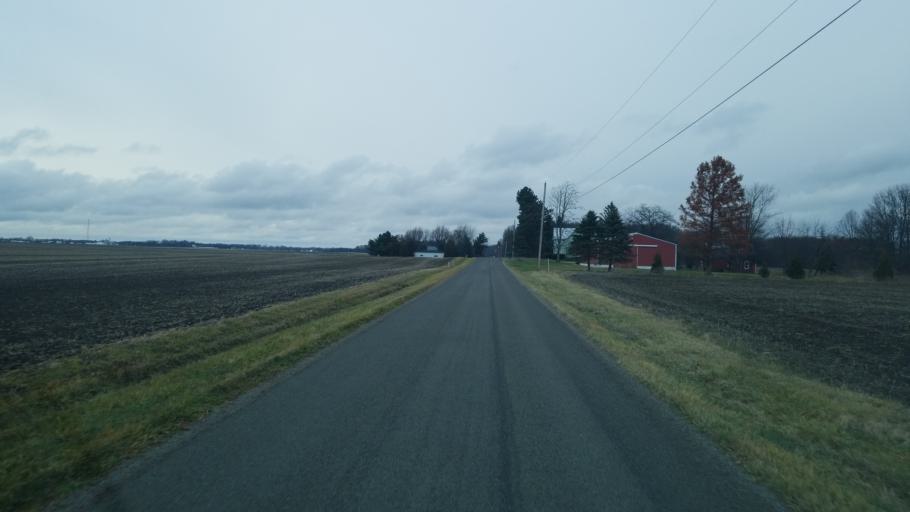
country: US
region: Ohio
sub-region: Union County
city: Richwood
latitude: 40.3165
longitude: -83.2512
